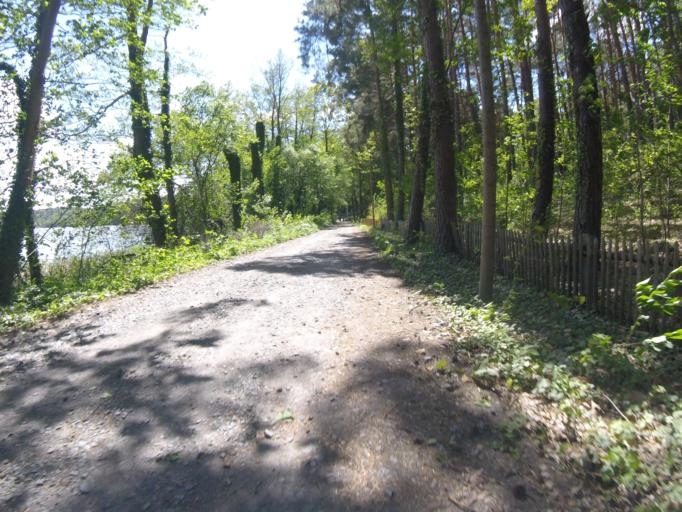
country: DE
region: Brandenburg
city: Teupitz
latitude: 52.1179
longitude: 13.6106
